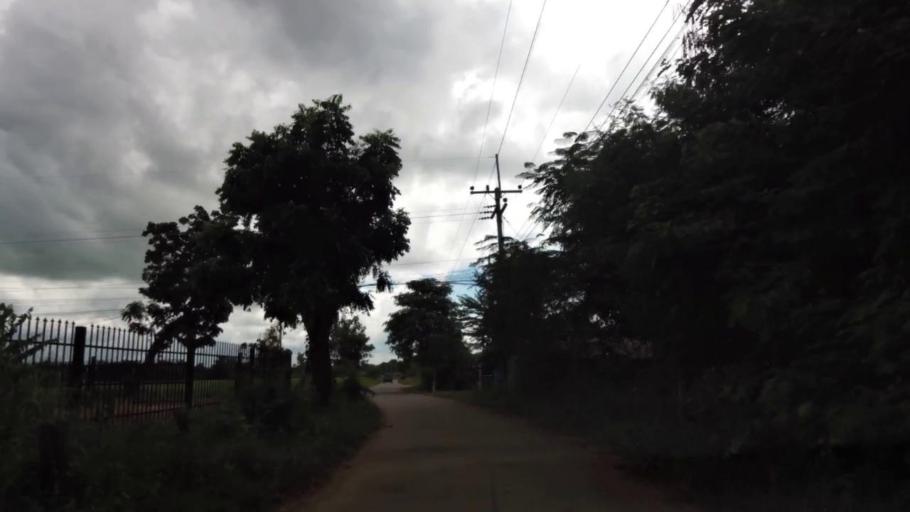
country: TH
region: Nakhon Sawan
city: Phai Sali
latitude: 15.6040
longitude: 100.6678
